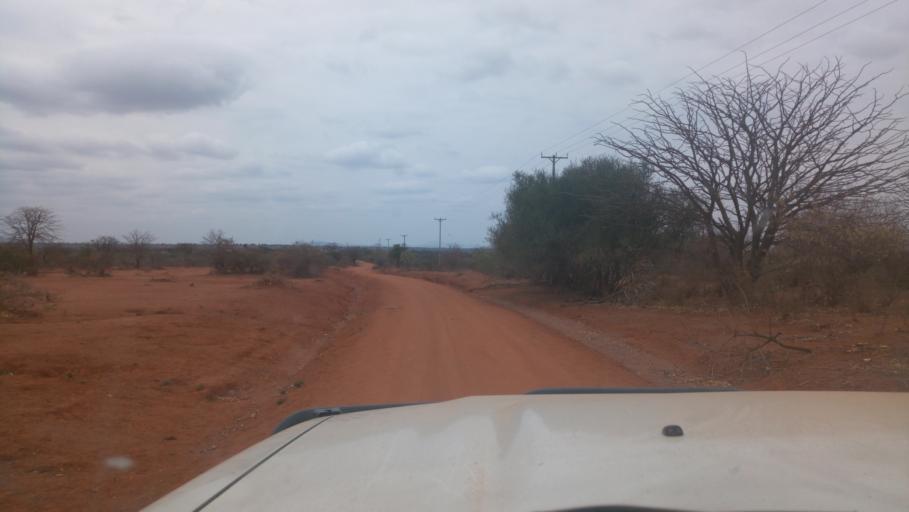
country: KE
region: Makueni
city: Wote
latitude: -1.8435
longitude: 38.0179
